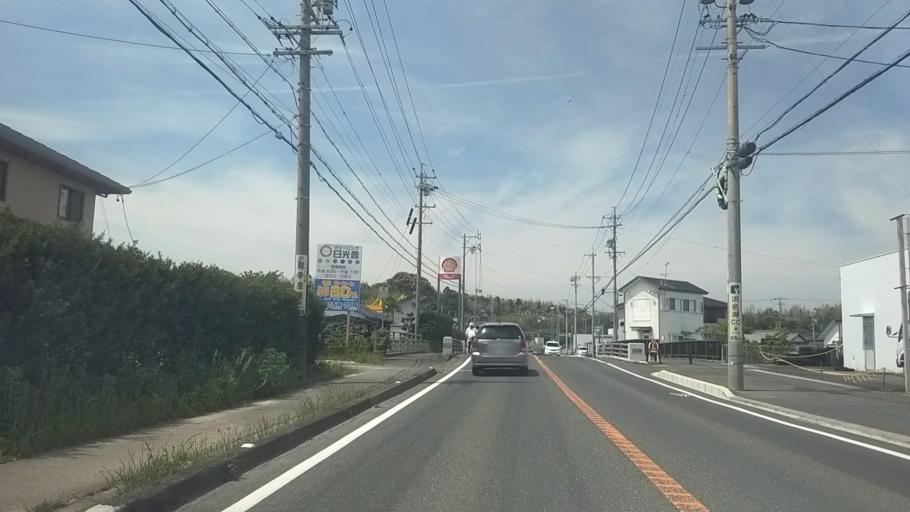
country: JP
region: Shizuoka
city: Kosai-shi
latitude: 34.7276
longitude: 137.5247
